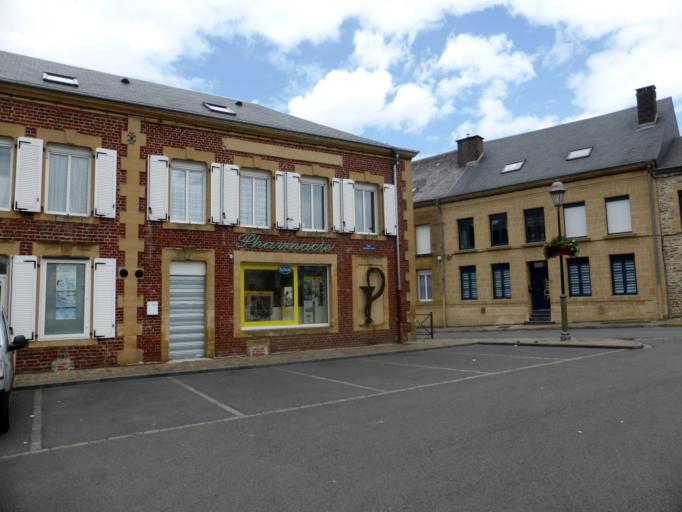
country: FR
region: Champagne-Ardenne
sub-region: Departement des Ardennes
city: Montherme
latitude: 49.8852
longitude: 4.7382
